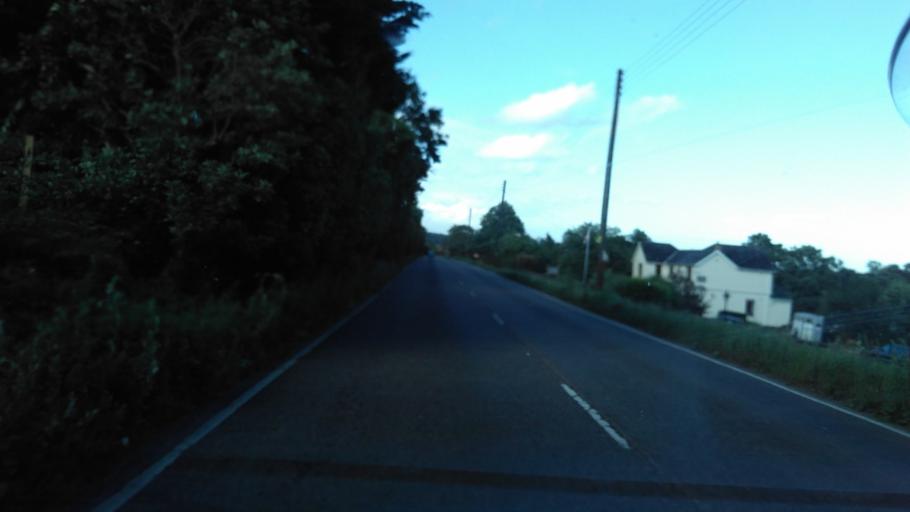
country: GB
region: England
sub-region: Kent
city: Chartham
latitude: 51.2507
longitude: 0.9868
